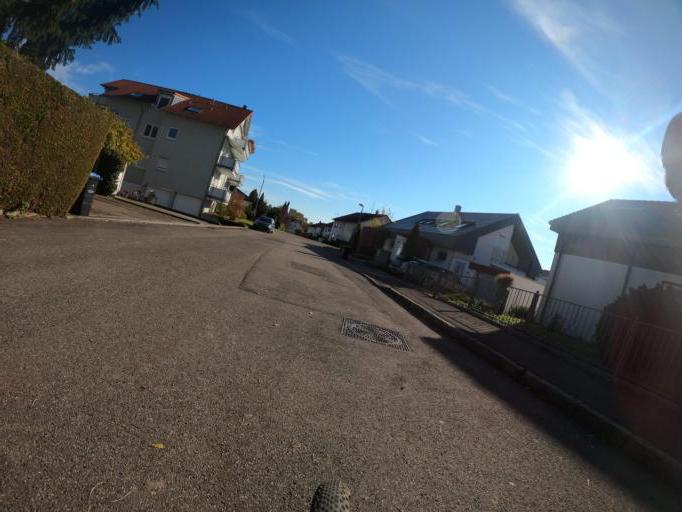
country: DE
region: Baden-Wuerttemberg
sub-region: Regierungsbezirk Stuttgart
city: Magstadt
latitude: 48.7205
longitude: 8.9588
